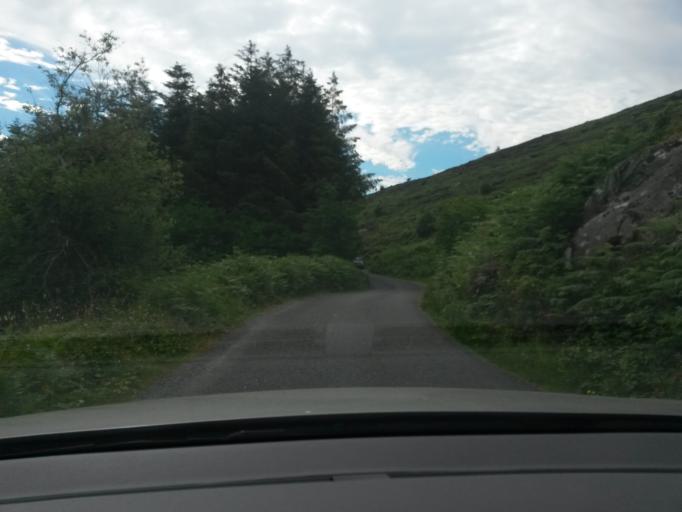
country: IE
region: Leinster
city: Ballinteer
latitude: 53.1829
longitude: -6.2763
